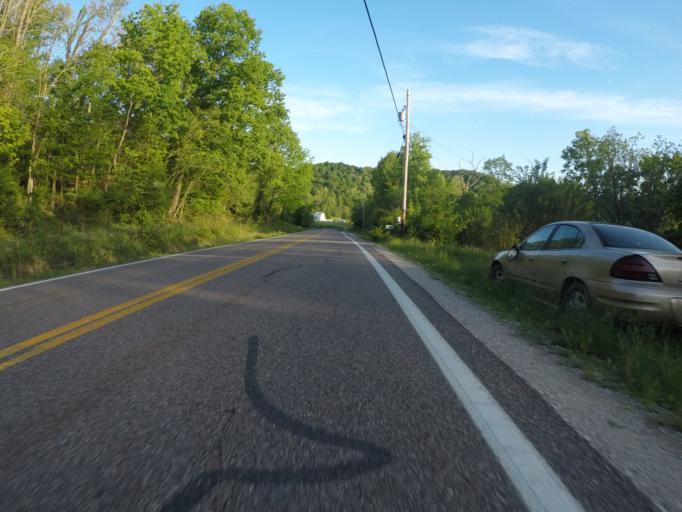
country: US
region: West Virginia
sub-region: Cabell County
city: Huntington
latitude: 38.5151
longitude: -82.4745
